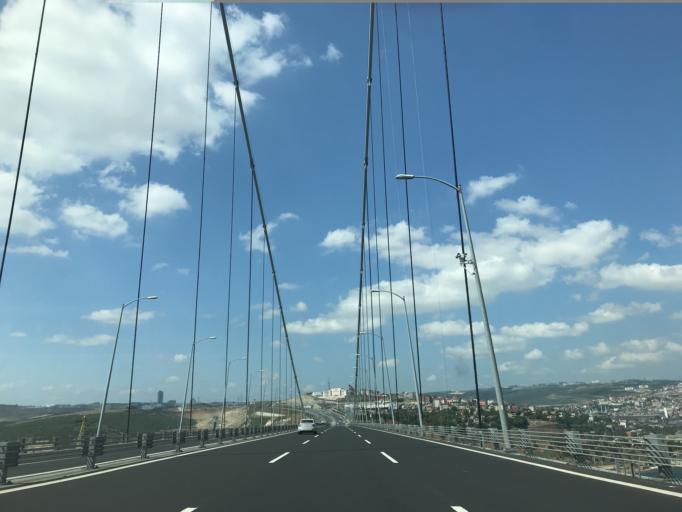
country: TR
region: Kocaeli
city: Tavsancil
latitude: 40.7628
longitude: 29.5173
